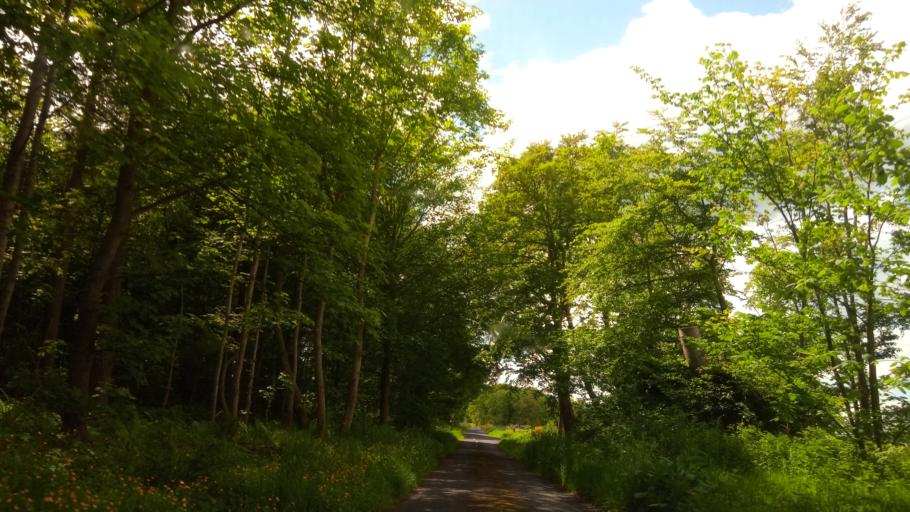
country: GB
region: Scotland
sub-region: The Scottish Borders
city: Coldstream
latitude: 55.5919
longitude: -2.2888
